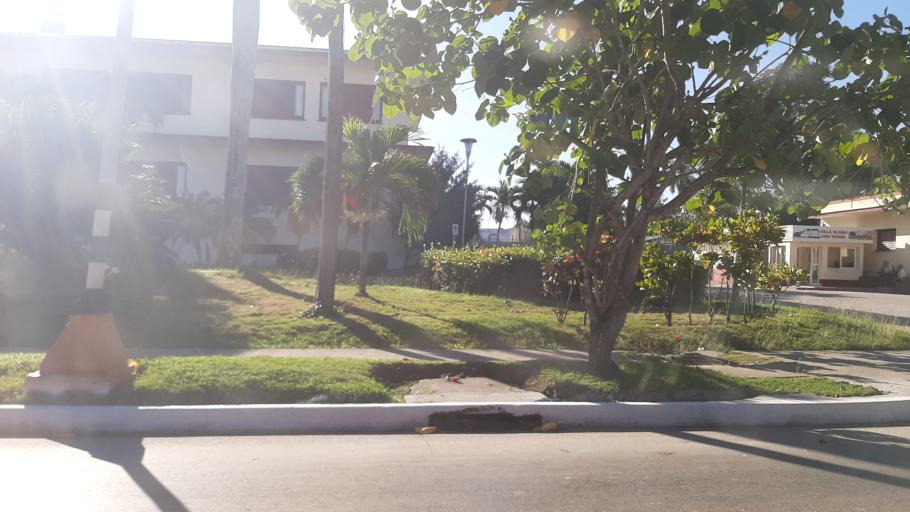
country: CU
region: Villa Clara
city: Santa Clara
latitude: 22.4119
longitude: -79.9570
